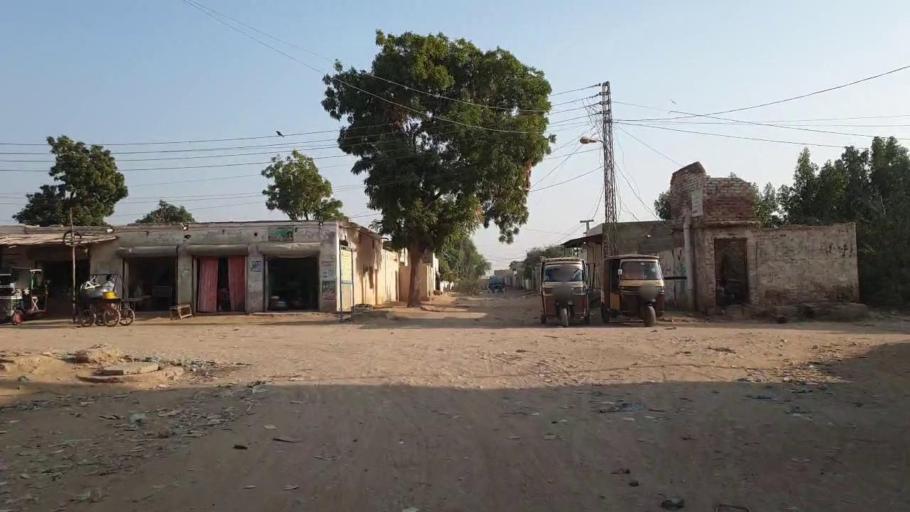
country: PK
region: Sindh
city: Kotri
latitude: 25.3584
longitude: 68.2596
